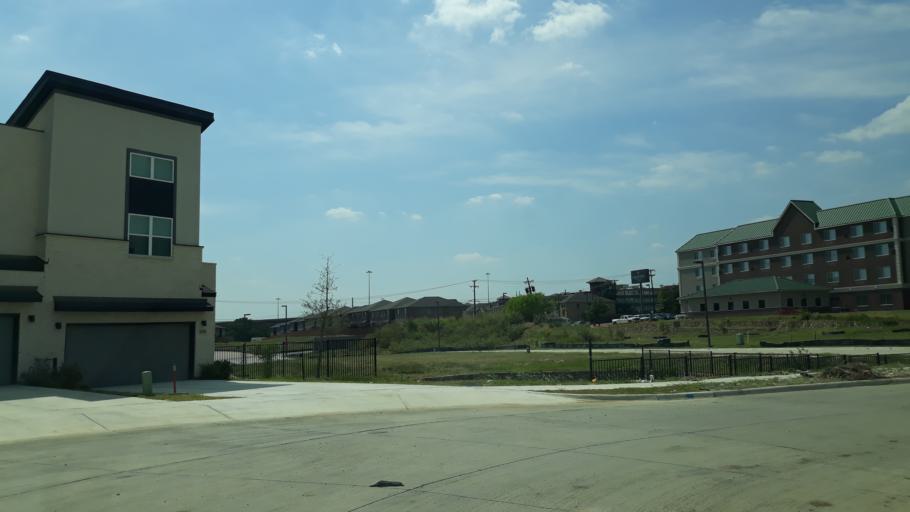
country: US
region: Texas
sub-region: Dallas County
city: Irving
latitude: 32.8337
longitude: -97.0115
